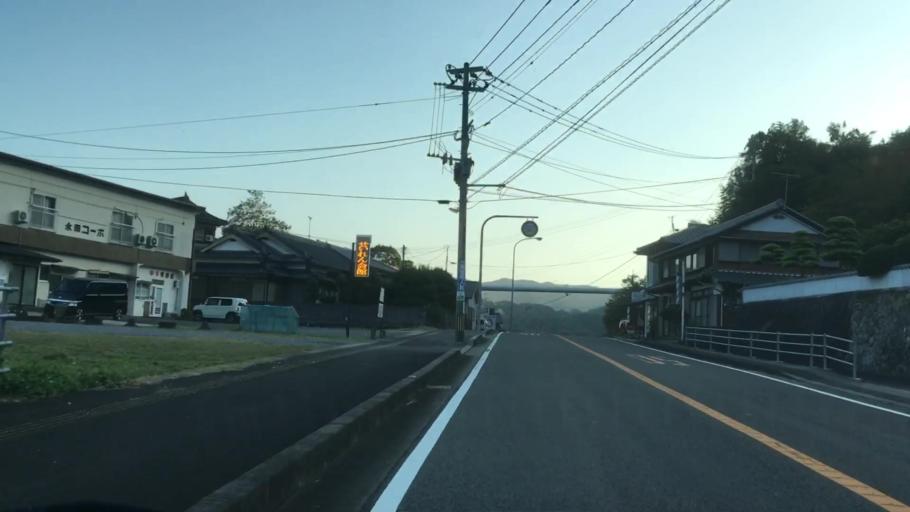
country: JP
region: Nagasaki
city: Sasebo
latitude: 33.0050
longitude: 129.7310
